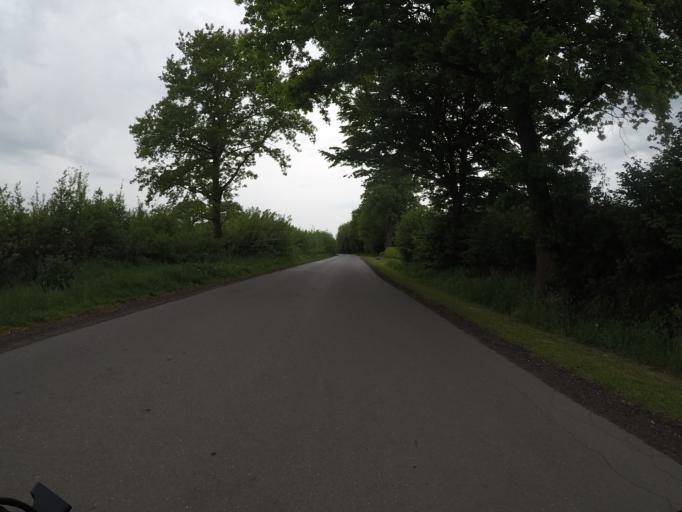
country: DE
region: Schleswig-Holstein
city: Kisdorf
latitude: 53.7842
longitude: 10.0167
